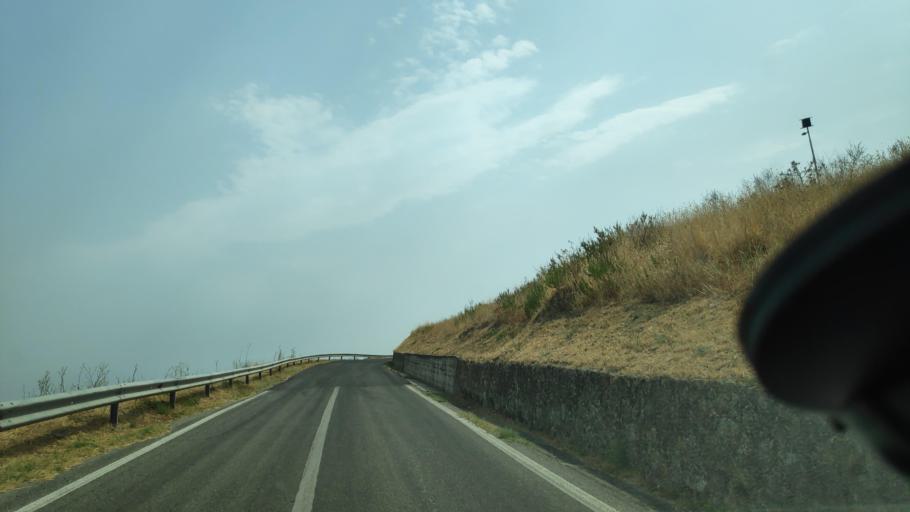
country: IT
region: Calabria
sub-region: Provincia di Catanzaro
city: Marina di Davoli
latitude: 38.6494
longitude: 16.5407
